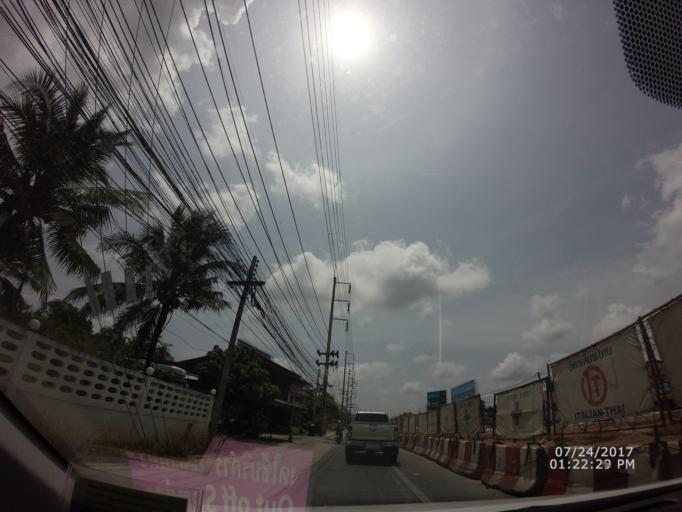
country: TH
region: Phuket
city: Thalang
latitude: 8.0916
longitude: 98.3393
